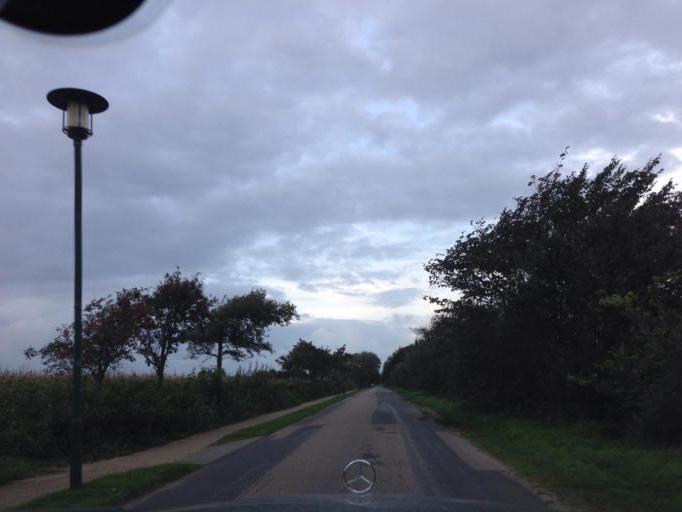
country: DE
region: Schleswig-Holstein
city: Nieblum
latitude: 54.6840
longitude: 8.4921
